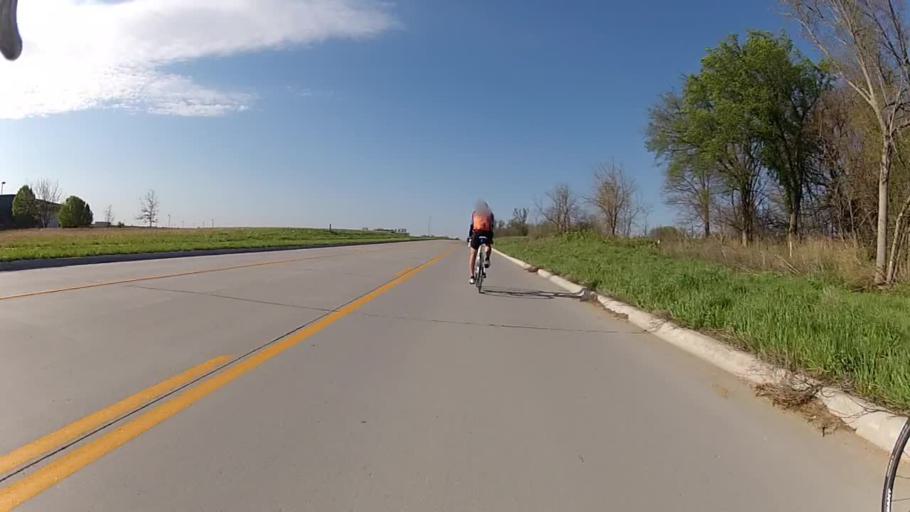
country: US
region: Kansas
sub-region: Riley County
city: Ogden
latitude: 39.1443
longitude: -96.6820
